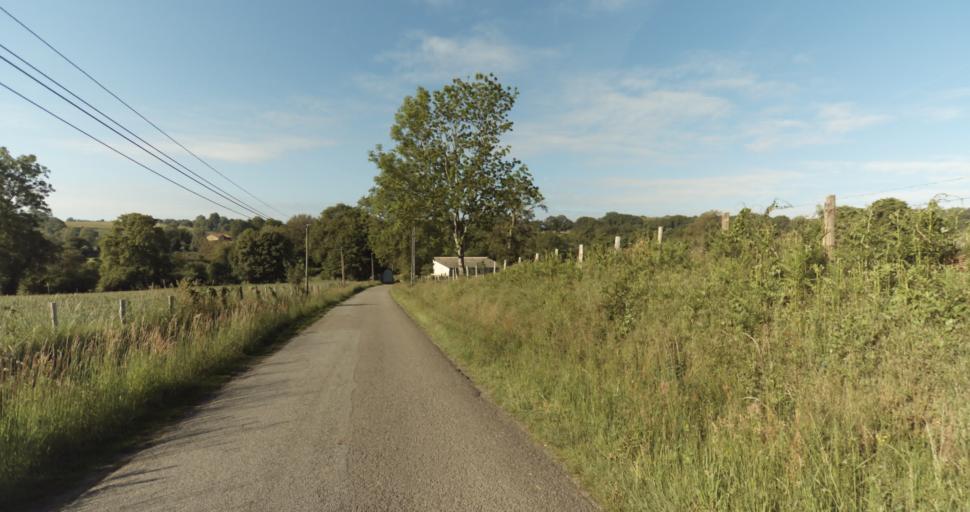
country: FR
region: Limousin
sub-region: Departement de la Haute-Vienne
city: Solignac
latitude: 45.7412
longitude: 1.2722
